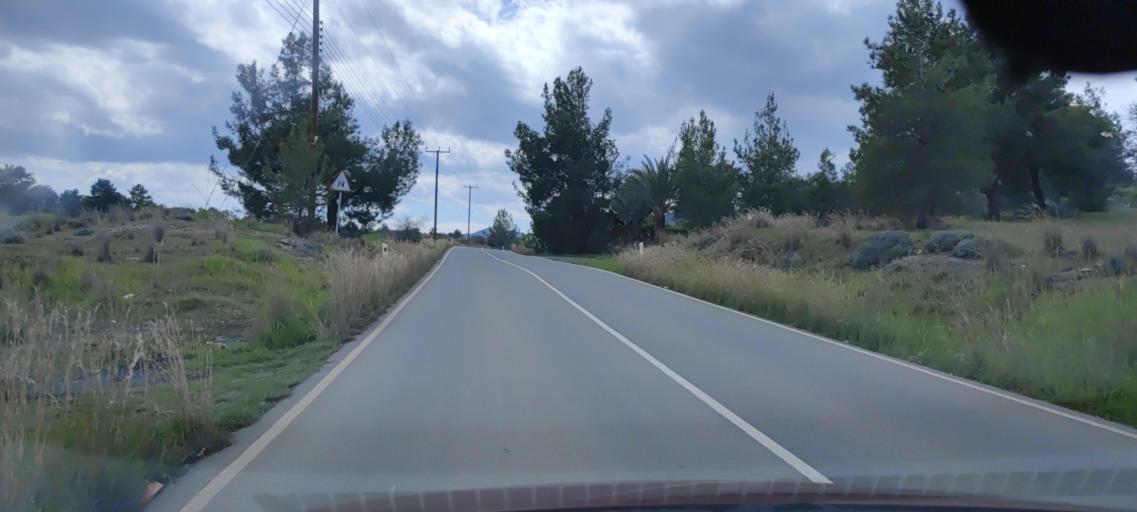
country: CY
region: Lefkosia
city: Lythrodontas
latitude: 34.9740
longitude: 33.2948
